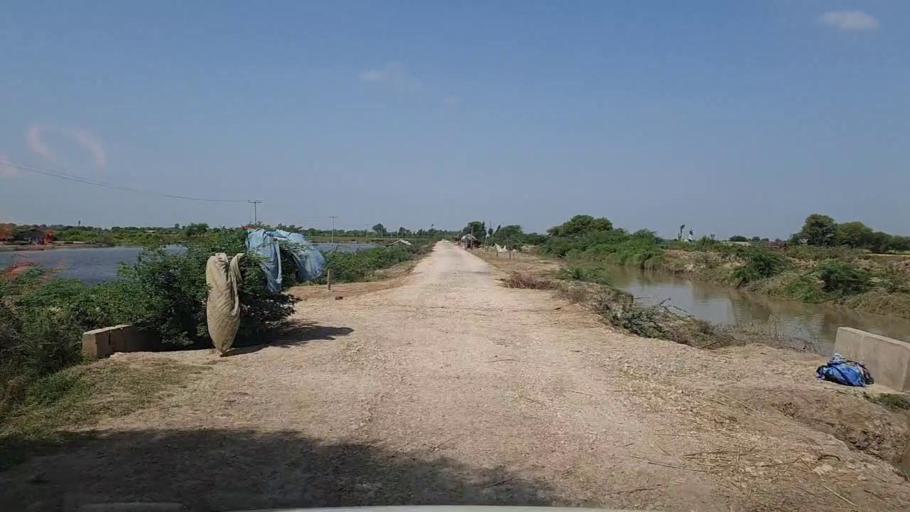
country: PK
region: Sindh
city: Kario
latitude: 24.8855
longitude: 68.6823
